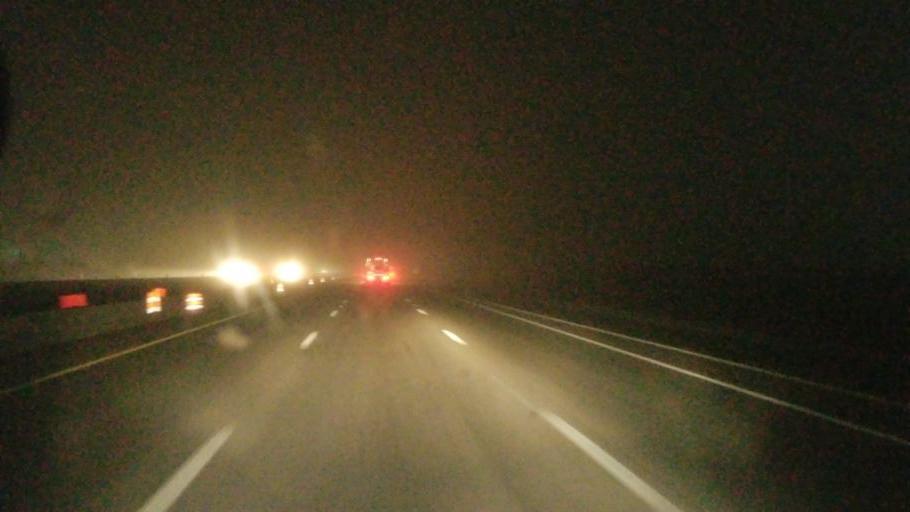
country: US
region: Ohio
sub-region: Franklin County
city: Columbus
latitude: 39.9109
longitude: -83.0204
